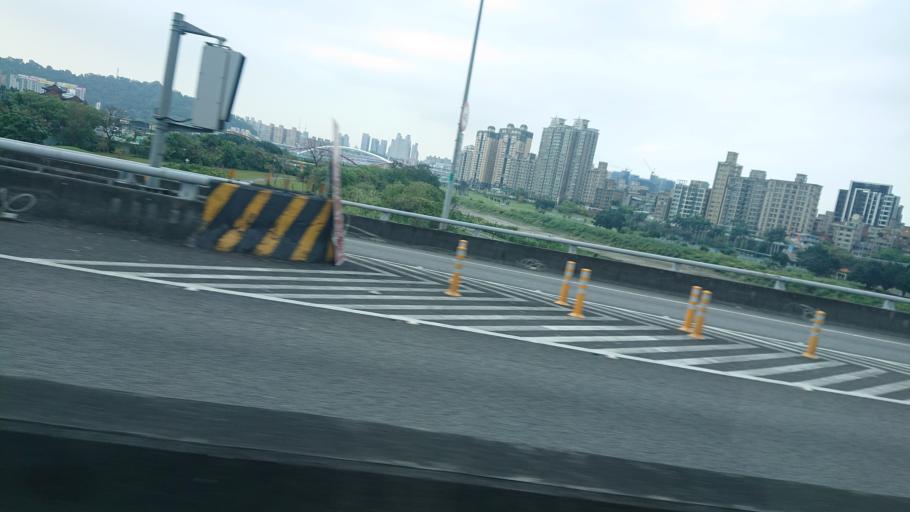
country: TW
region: Taipei
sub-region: Taipei
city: Banqiao
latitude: 24.9698
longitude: 121.5263
